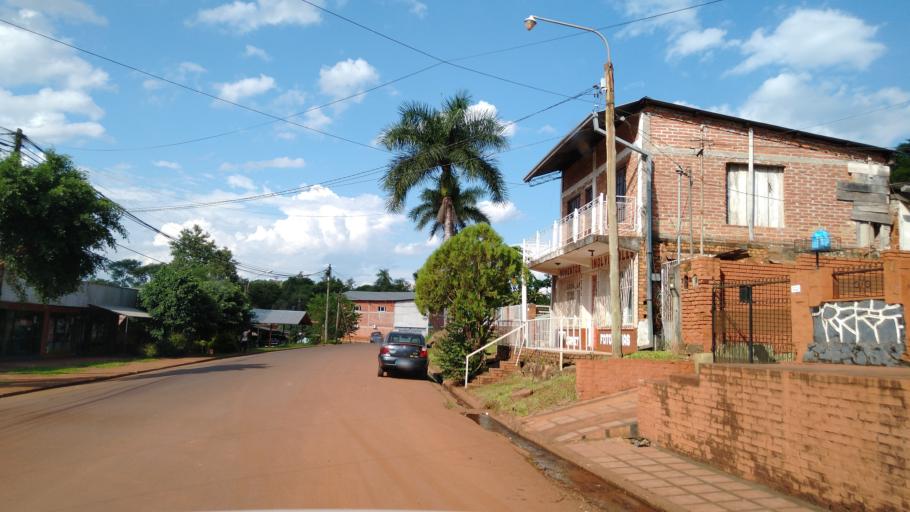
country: AR
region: Misiones
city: Puerto Piray
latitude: -26.4683
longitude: -54.7150
